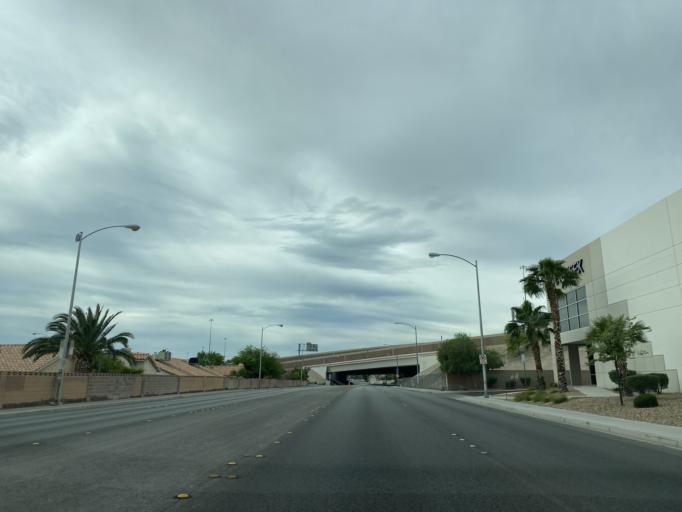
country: US
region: Nevada
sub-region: Clark County
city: Paradise
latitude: 36.0605
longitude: -115.1411
